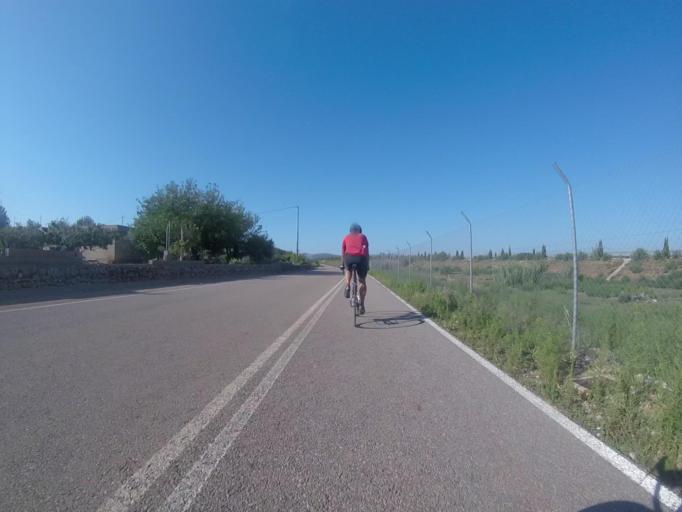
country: ES
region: Valencia
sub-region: Provincia de Castello
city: Benlloch
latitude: 40.1931
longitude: 0.0499
